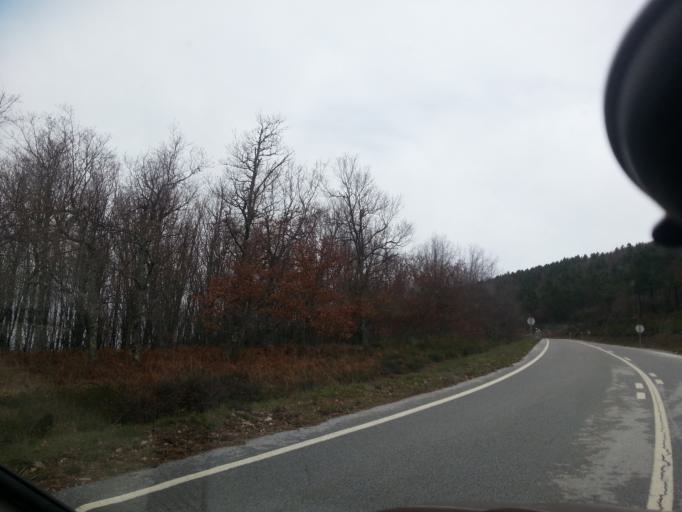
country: PT
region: Guarda
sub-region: Seia
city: Seia
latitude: 40.3412
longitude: -7.7135
